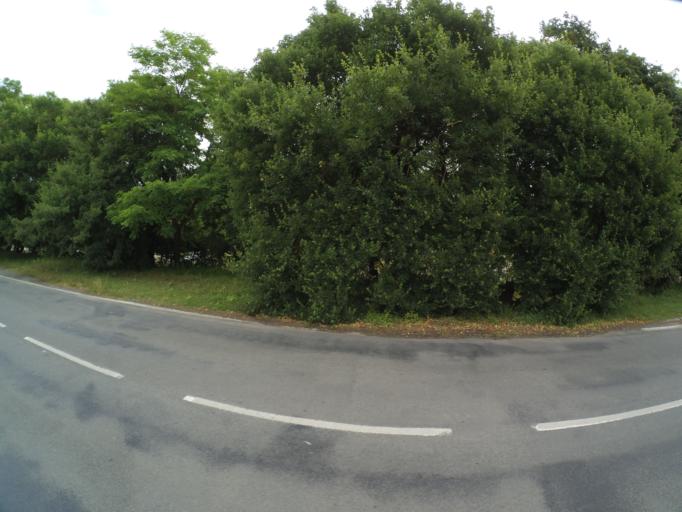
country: FR
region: Poitou-Charentes
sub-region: Departement de la Charente-Maritime
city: Saint-Laurent-de-la-Pree
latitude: 45.9926
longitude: -1.0278
